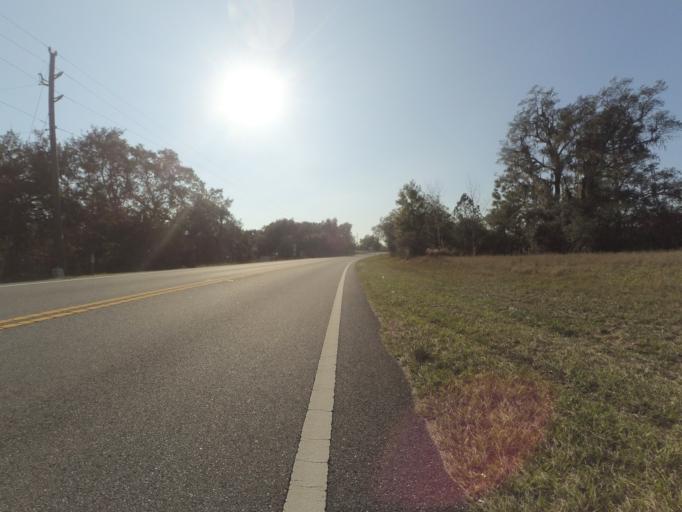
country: US
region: Florida
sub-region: Lake County
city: Umatilla
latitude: 28.9814
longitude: -81.7422
